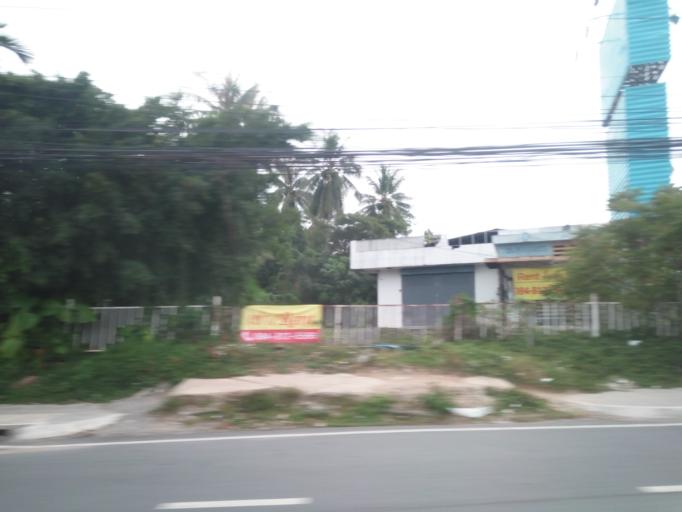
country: TH
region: Phuket
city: Ban Ko Kaeo
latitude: 7.9585
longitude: 98.3843
